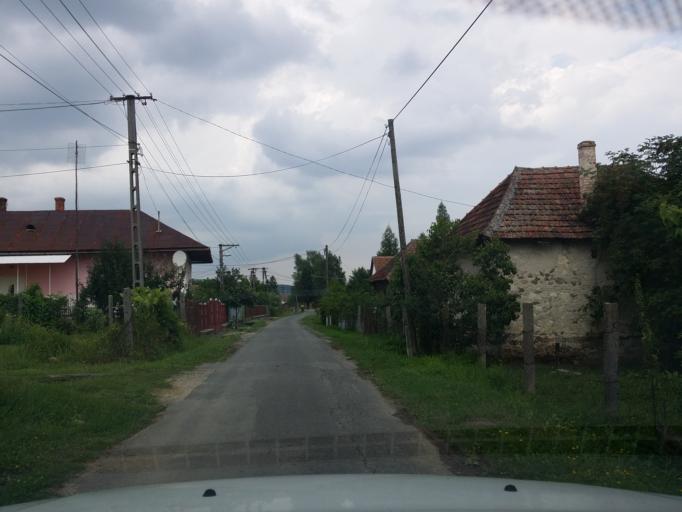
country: HU
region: Borsod-Abauj-Zemplen
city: Sarospatak
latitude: 48.4539
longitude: 21.5269
